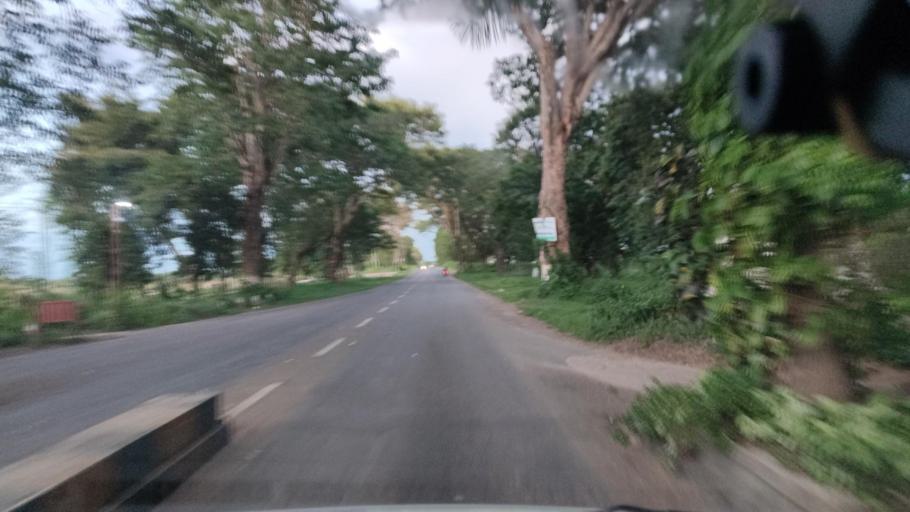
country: MM
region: Magway
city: Minbu
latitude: 20.2106
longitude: 94.8467
